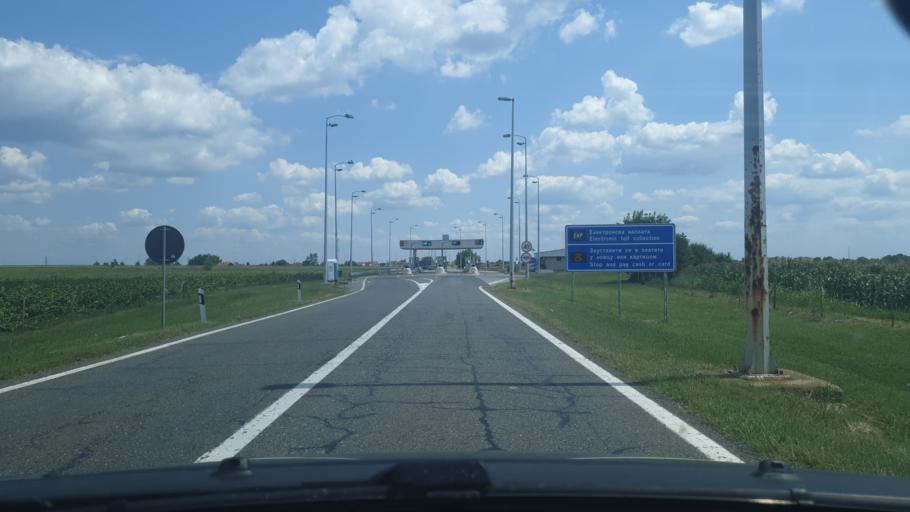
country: RS
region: Autonomna Pokrajina Vojvodina
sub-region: Sremski Okrug
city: Pecinci
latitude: 44.9193
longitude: 19.9514
